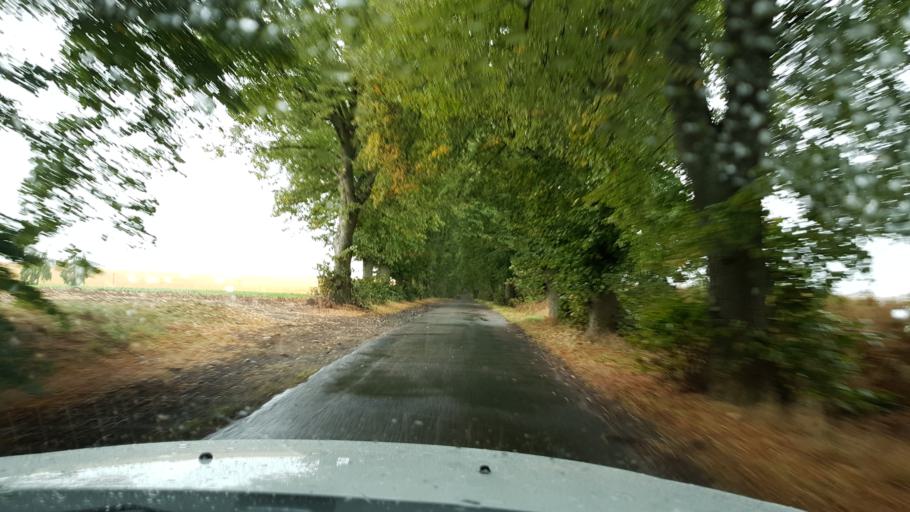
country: DE
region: Brandenburg
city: Schwedt (Oder)
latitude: 53.0144
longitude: 14.3076
